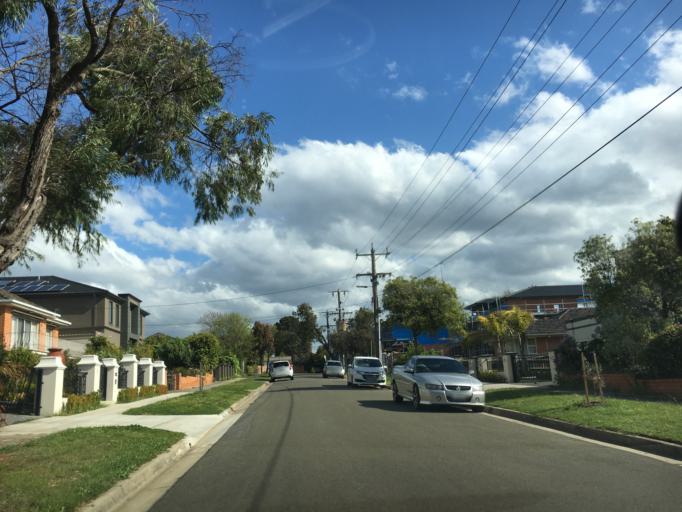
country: AU
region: Victoria
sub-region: Whitehorse
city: Vermont South
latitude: -37.8850
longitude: 145.1721
